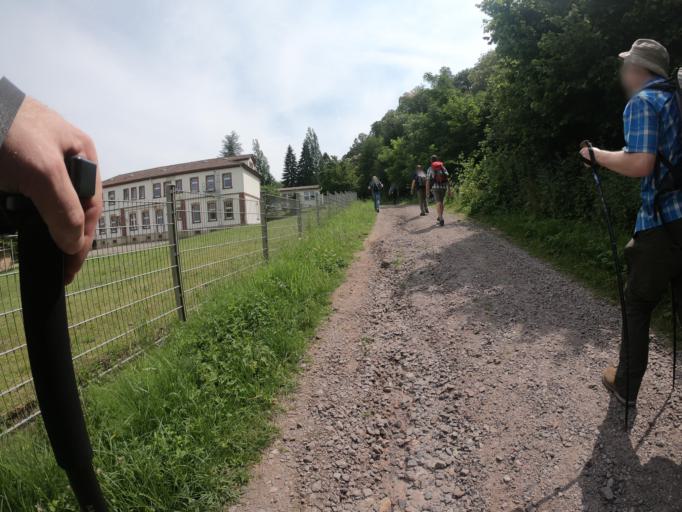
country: DE
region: Rheinland-Pfalz
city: Klingenmunster
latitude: 49.1524
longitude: 8.0108
